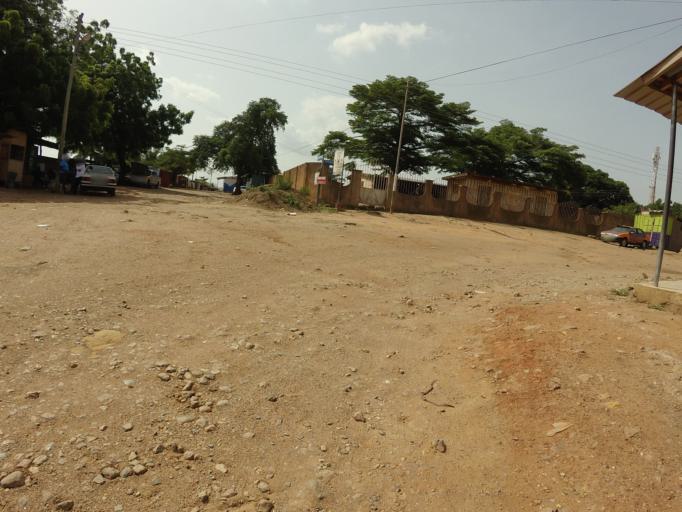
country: GH
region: Greater Accra
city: Dome
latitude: 5.6098
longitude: -0.2415
